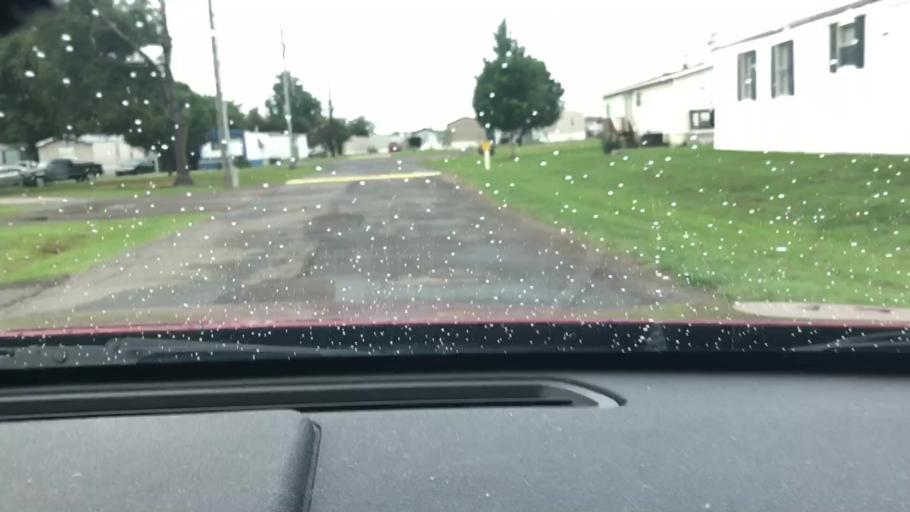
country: US
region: Texas
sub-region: Bowie County
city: Nash
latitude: 33.4428
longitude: -94.1394
